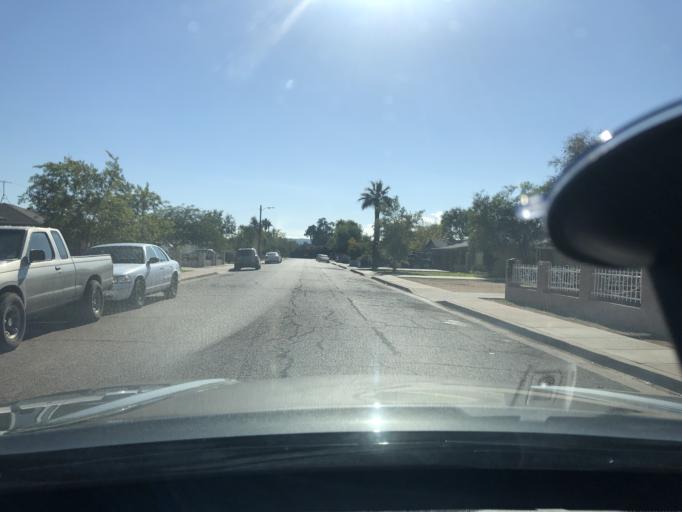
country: US
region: Arizona
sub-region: Maricopa County
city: Phoenix
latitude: 33.4701
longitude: -112.0290
